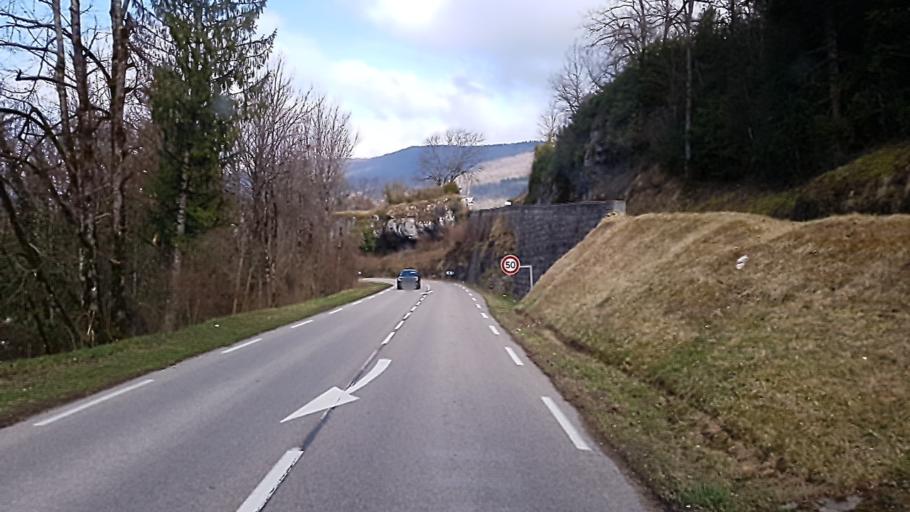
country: FR
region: Rhone-Alpes
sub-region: Departement de l'Ain
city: Dortan
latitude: 46.3221
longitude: 5.6648
